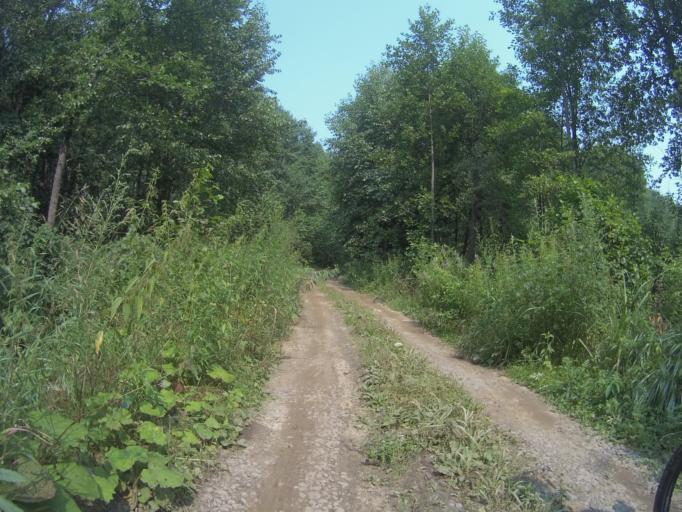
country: RU
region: Vladimir
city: Vorsha
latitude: 55.9770
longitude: 40.1869
